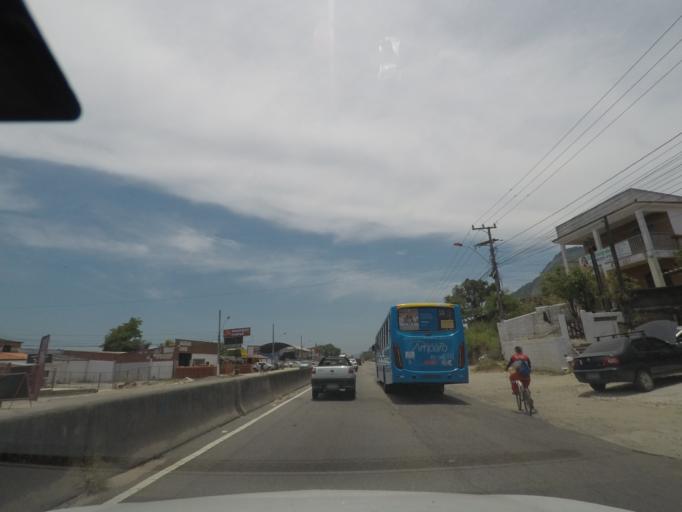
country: BR
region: Rio de Janeiro
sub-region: Marica
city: Marica
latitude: -22.9333
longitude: -42.8929
